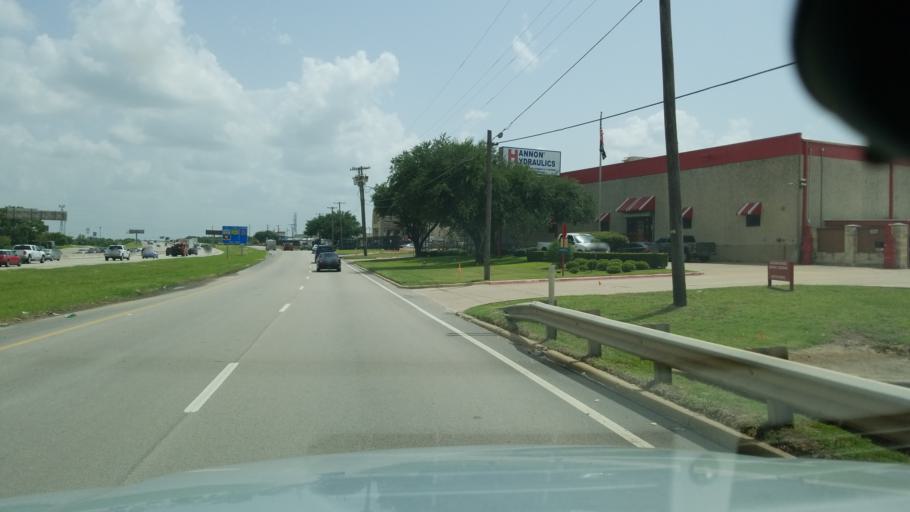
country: US
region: Texas
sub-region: Dallas County
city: Irving
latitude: 32.8211
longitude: -96.9214
